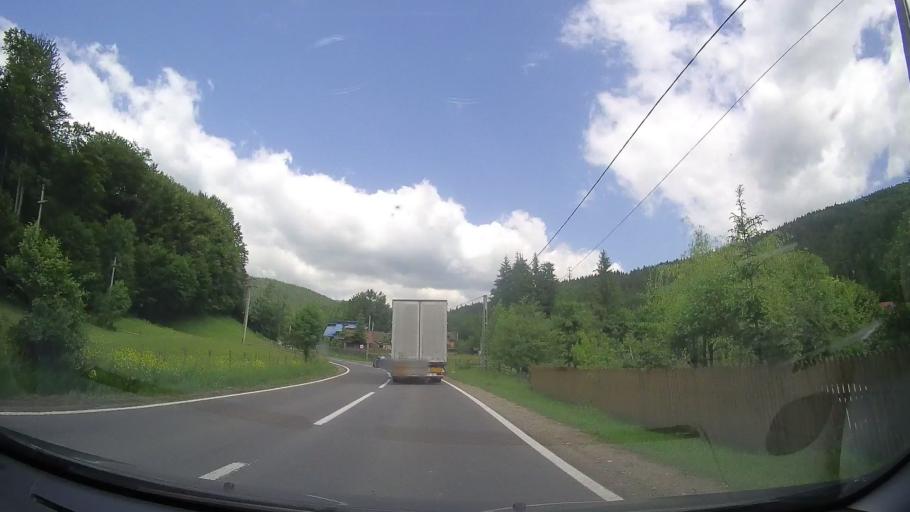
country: RO
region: Prahova
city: Maneciu
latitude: 45.3609
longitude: 25.9408
